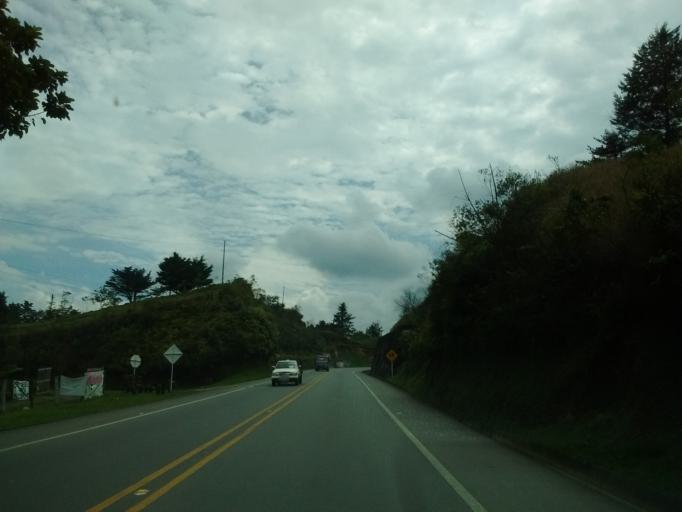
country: CO
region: Cauca
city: Cajibio
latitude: 2.5495
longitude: -76.5650
